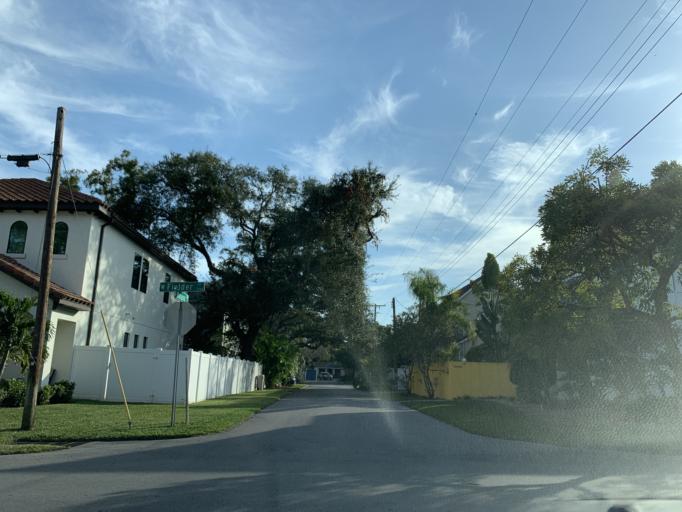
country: US
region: Florida
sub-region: Hillsborough County
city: Tampa
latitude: 27.8967
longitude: -82.4967
